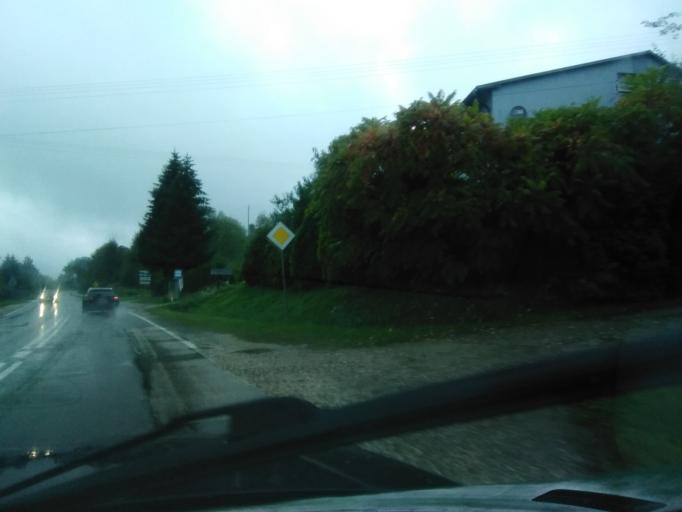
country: PL
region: Subcarpathian Voivodeship
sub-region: Powiat ropczycko-sedziszowski
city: Niedzwiada
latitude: 50.0097
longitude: 21.5538
